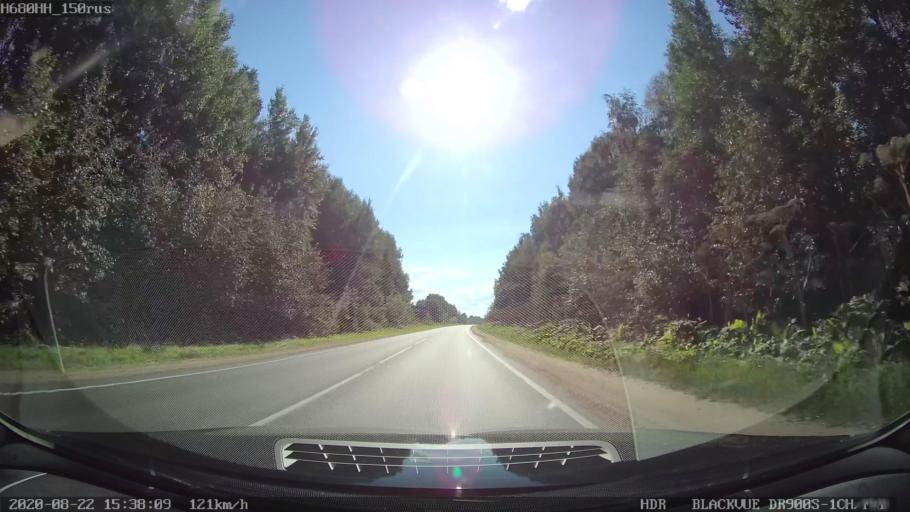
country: RU
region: Tverskaya
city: Bezhetsk
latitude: 57.7652
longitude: 36.6569
